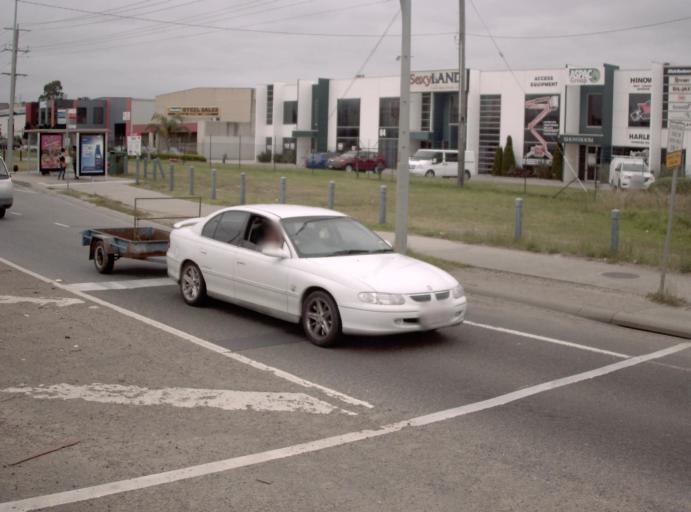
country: AU
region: Victoria
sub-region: Casey
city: Hallam
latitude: -38.0178
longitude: 145.2708
